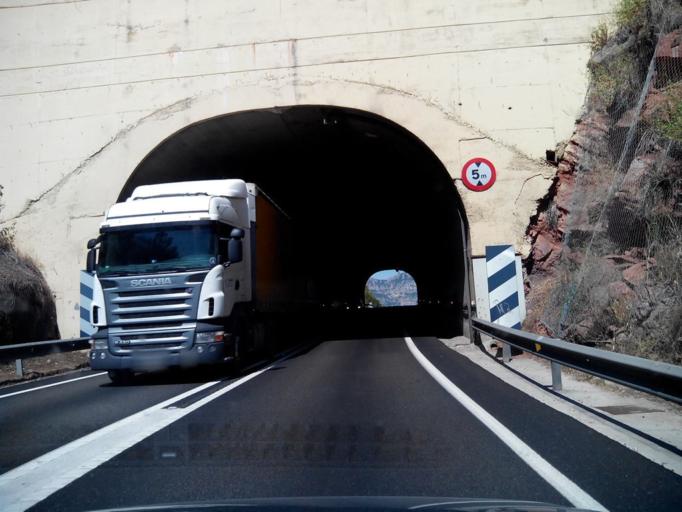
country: ES
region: Catalonia
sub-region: Provincia de Barcelona
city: Viladecavalls
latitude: 41.5833
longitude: 1.9449
